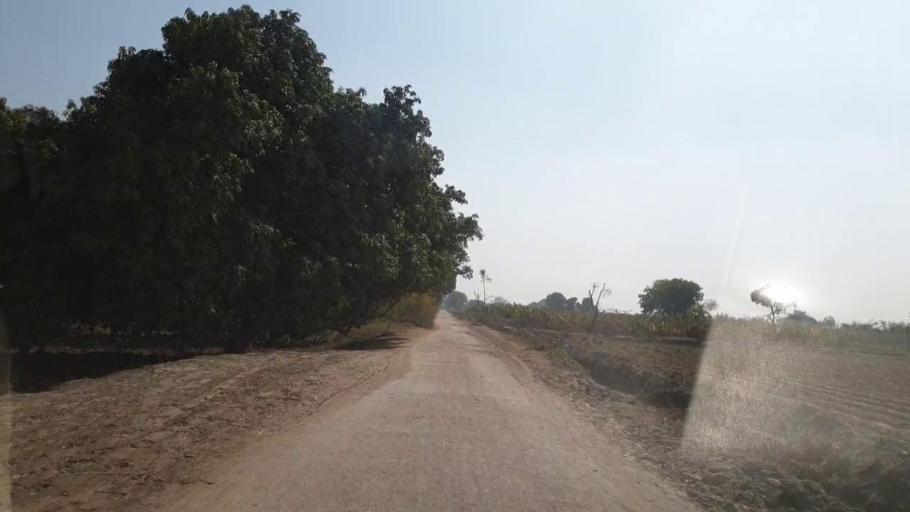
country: PK
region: Sindh
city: Matiari
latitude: 25.5097
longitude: 68.4628
